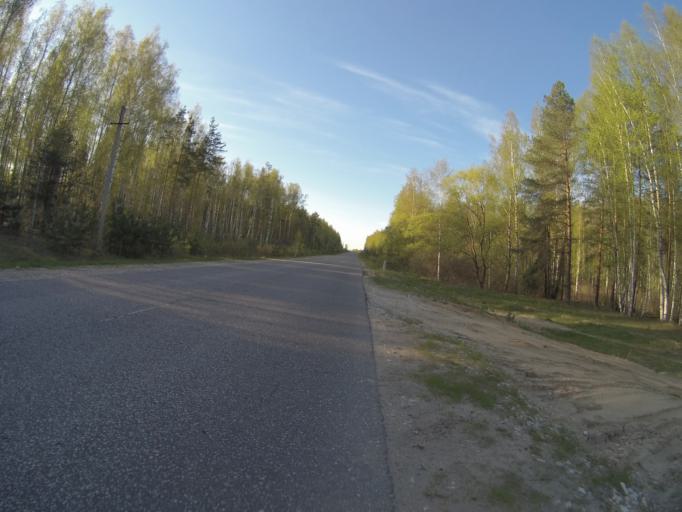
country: RU
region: Vladimir
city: Sudogda
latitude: 56.0921
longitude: 40.7863
